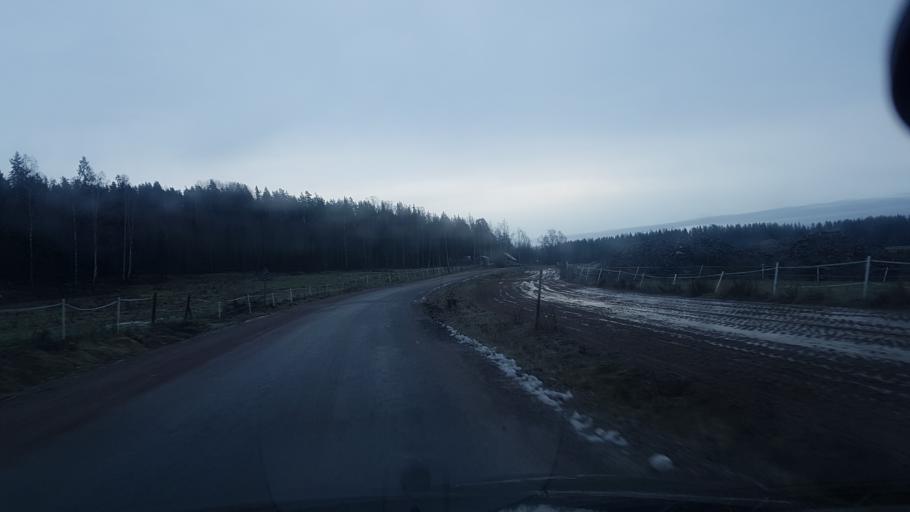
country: SE
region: Dalarna
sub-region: Borlange Kommun
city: Ornas
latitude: 60.4433
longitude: 15.6435
